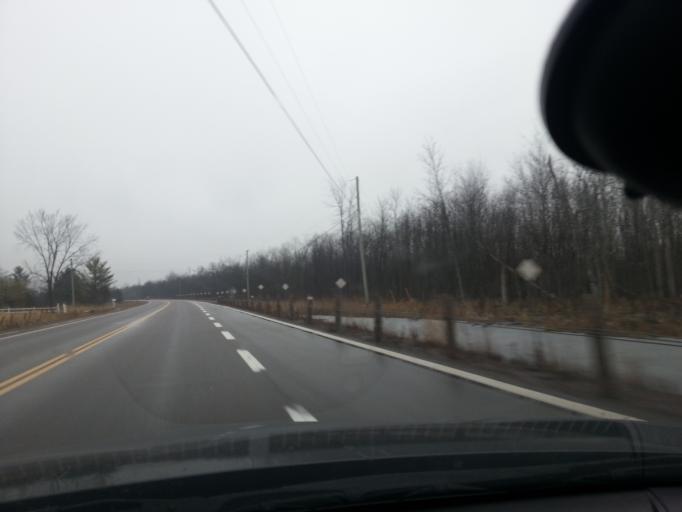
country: CA
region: Ontario
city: Belleville
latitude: 44.5568
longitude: -77.2843
